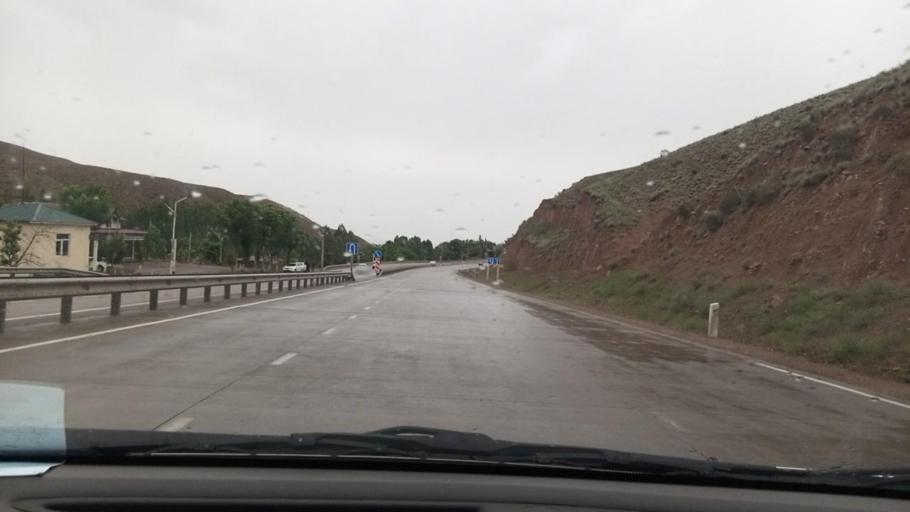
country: UZ
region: Namangan
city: Pop Shahri
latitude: 40.9507
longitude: 70.6779
